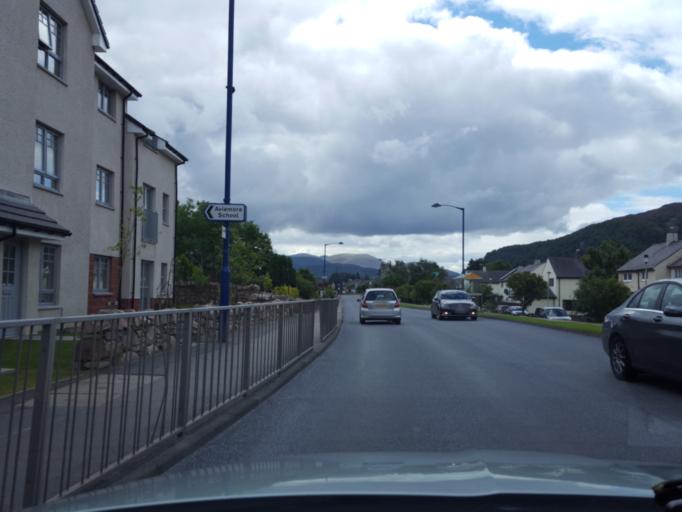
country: GB
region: Scotland
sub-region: Highland
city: Aviemore
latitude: 57.1984
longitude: -3.8288
